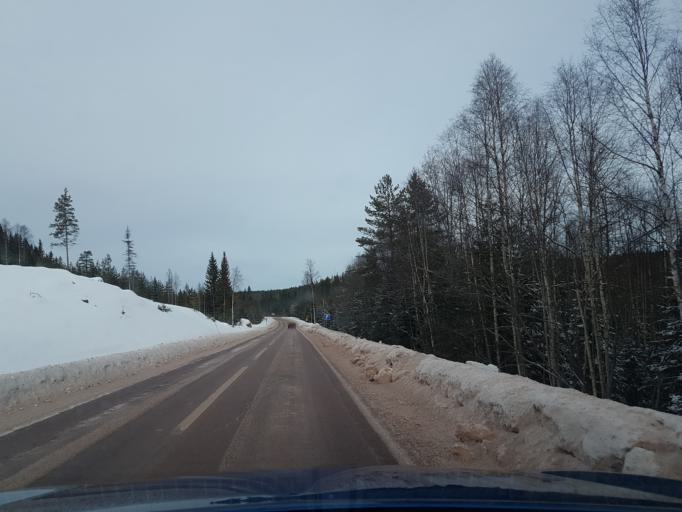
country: SE
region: Dalarna
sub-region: Orsa Kommun
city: Orsa
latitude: 61.3143
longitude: 14.7198
